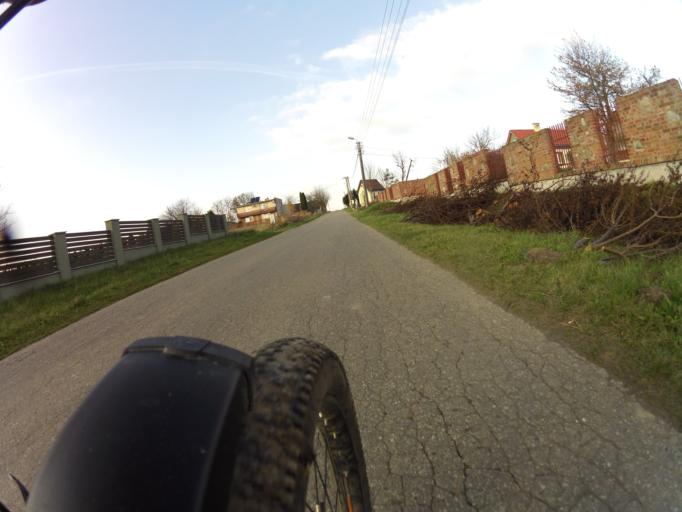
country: PL
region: Pomeranian Voivodeship
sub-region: Powiat pucki
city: Krokowa
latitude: 54.7619
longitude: 18.1821
